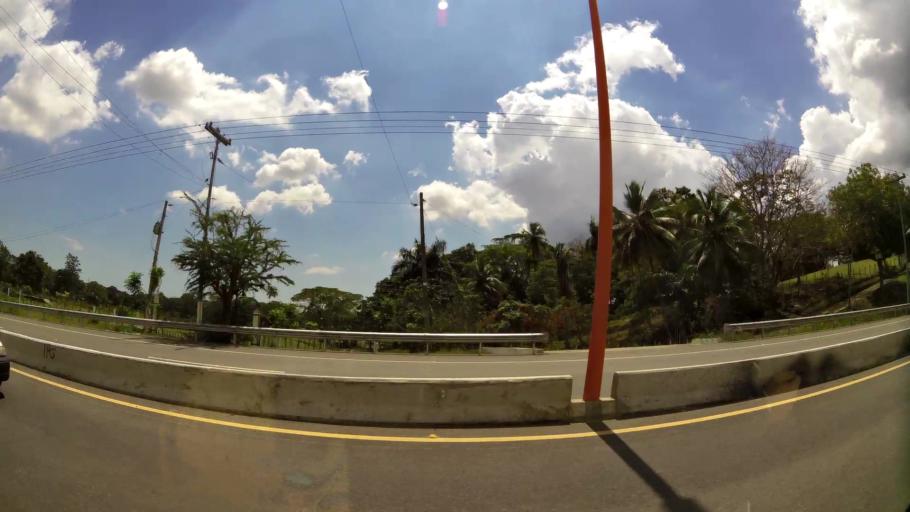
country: DO
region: Nacional
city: Santo Domingo
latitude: 18.5432
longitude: -69.9613
